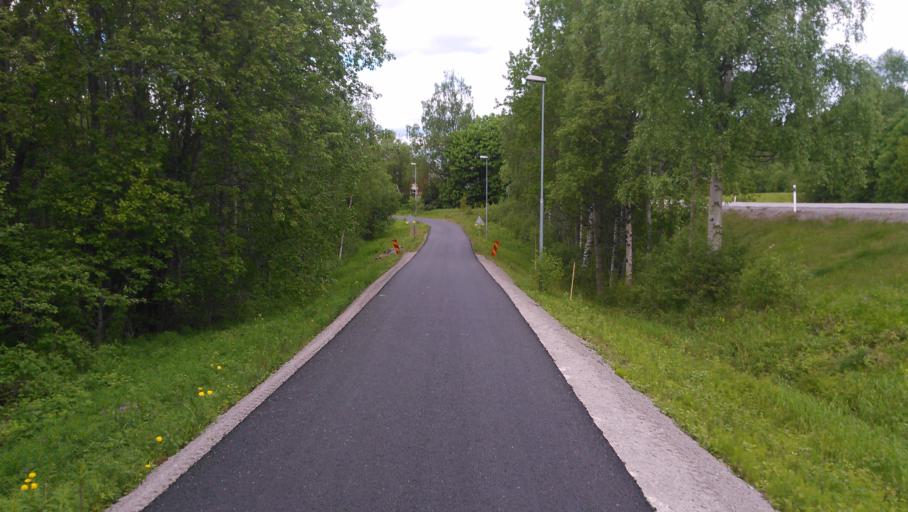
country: SE
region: Vaesterbotten
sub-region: Umea Kommun
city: Roback
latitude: 63.8570
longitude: 20.0940
